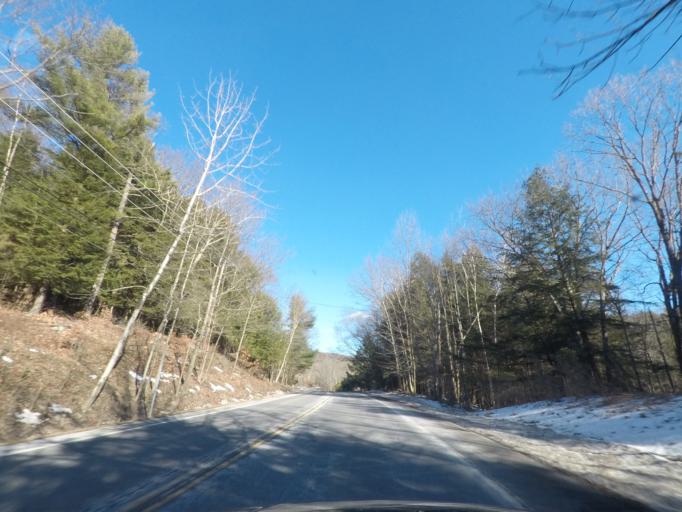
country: US
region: New York
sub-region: Columbia County
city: Chatham
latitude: 42.3192
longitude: -73.5148
